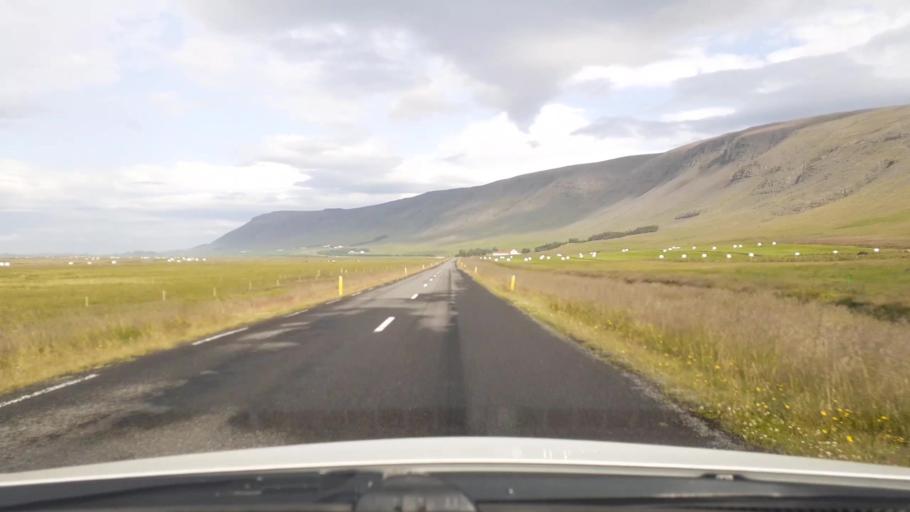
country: IS
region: Capital Region
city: Mosfellsbaer
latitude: 64.3283
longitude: -21.5079
